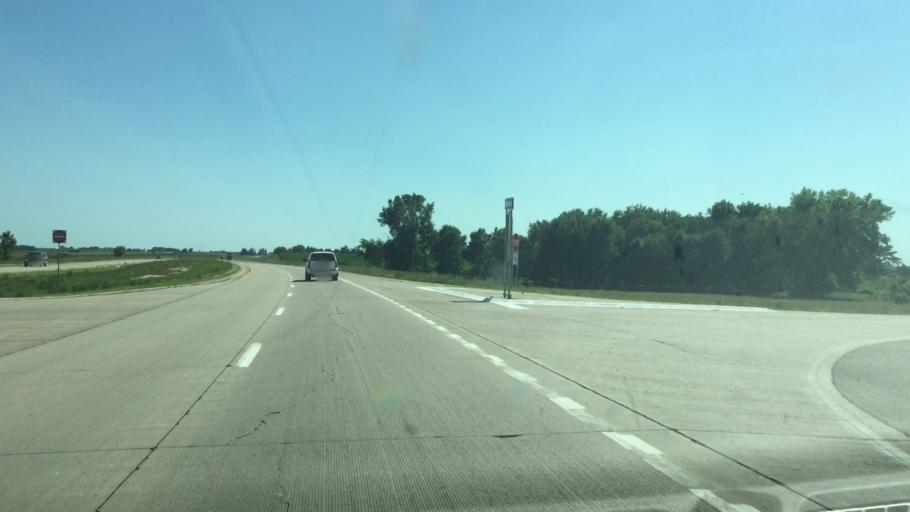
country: US
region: Iowa
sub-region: Jones County
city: Monticello
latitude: 42.1961
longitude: -91.2138
